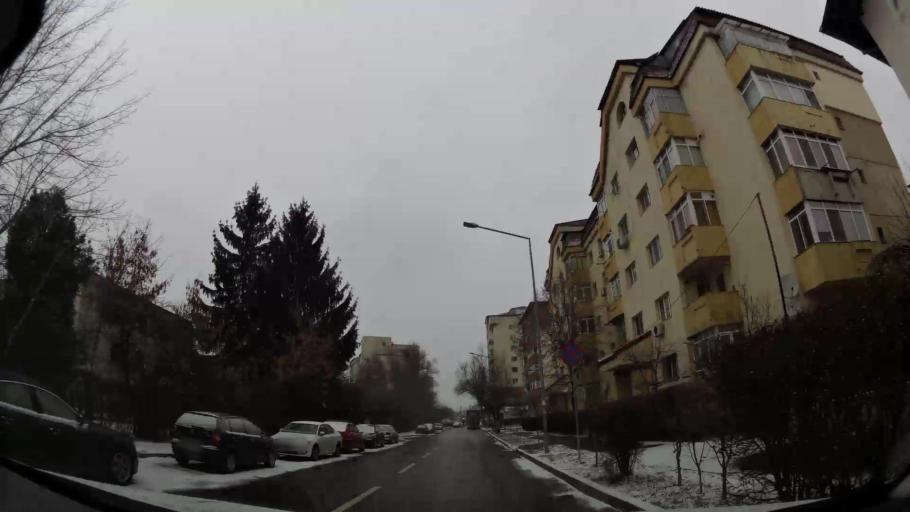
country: RO
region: Dambovita
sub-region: Municipiul Targoviste
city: Targoviste
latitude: 44.9169
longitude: 25.4671
